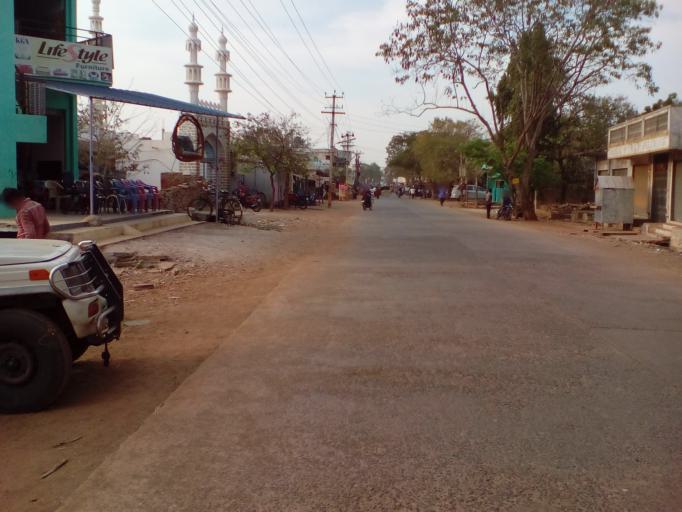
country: IN
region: Andhra Pradesh
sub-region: Kurnool
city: Nandikotkur
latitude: 15.8512
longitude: 78.2665
